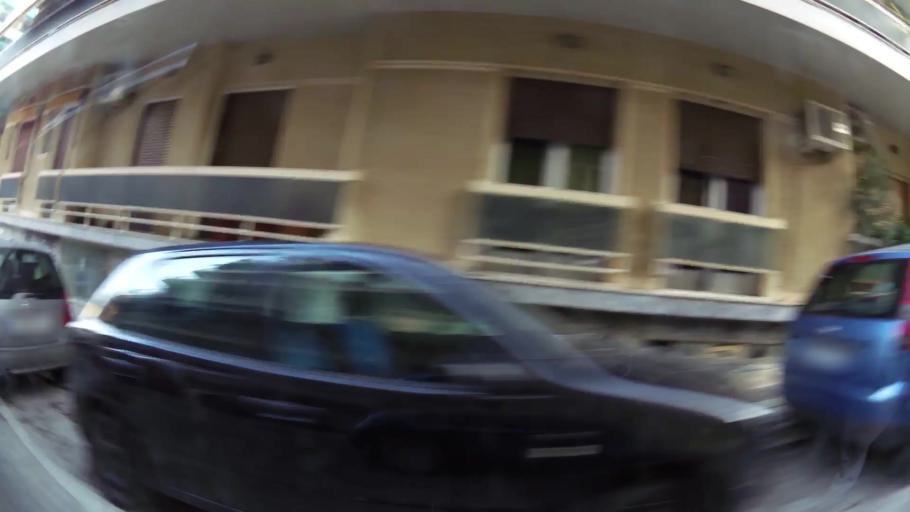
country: GR
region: Attica
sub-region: Nomarchia Athinas
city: Vyronas
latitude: 37.9729
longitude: 23.7561
